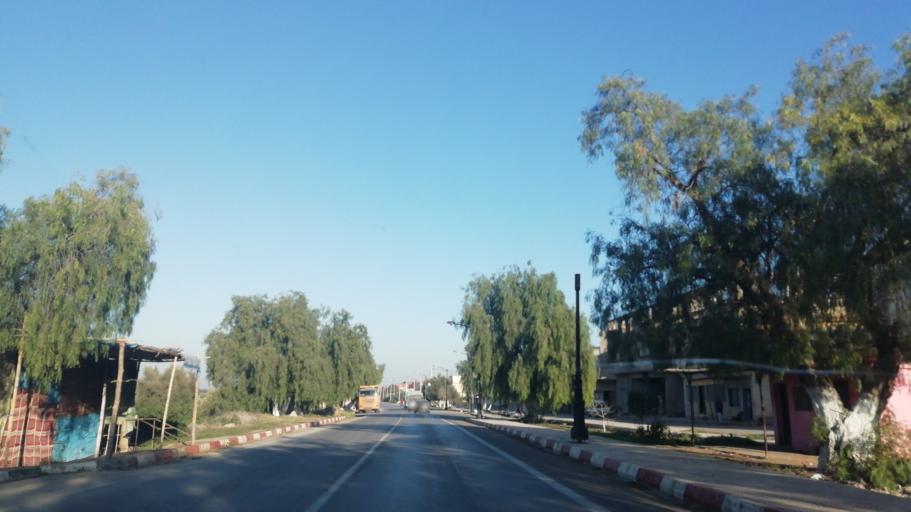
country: MA
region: Oriental
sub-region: Berkane-Taourirt
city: Ahfir
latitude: 34.9749
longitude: -2.1028
